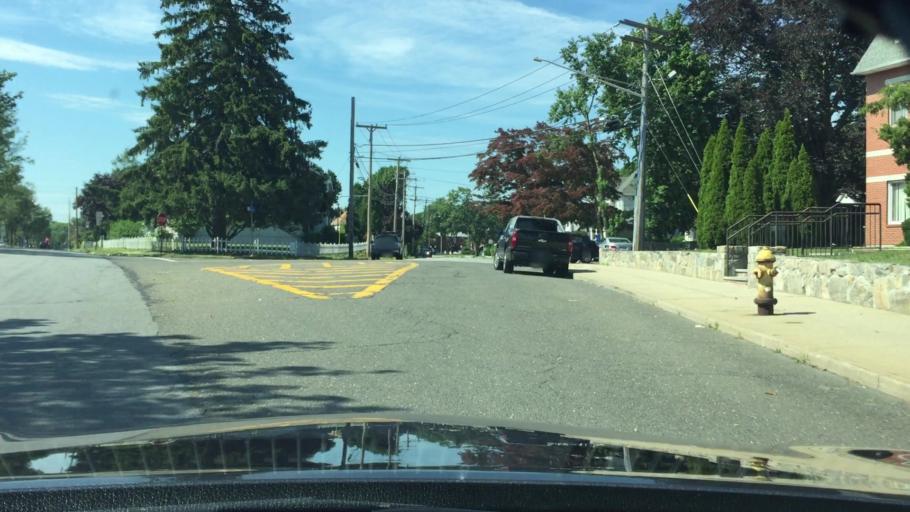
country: US
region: Connecticut
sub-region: Fairfield County
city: Trumbull
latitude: 41.2054
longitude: -73.2057
